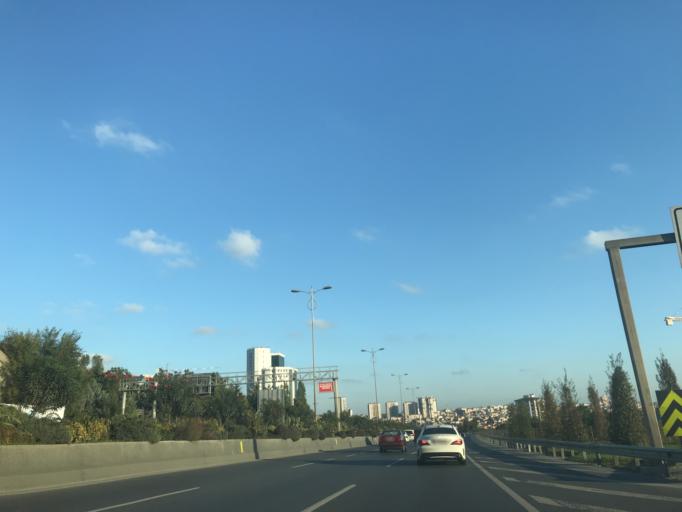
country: TR
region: Istanbul
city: Mahmutbey
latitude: 41.0607
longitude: 28.8423
